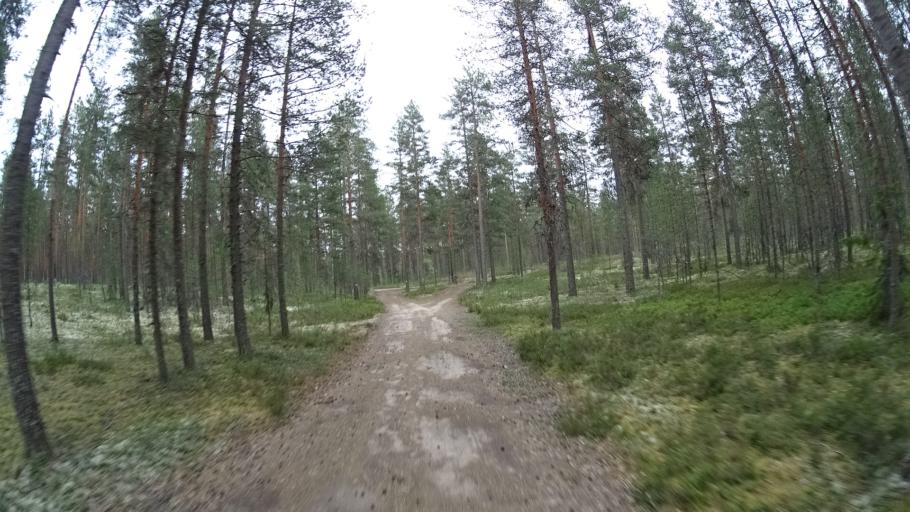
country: FI
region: Satakunta
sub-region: Pohjois-Satakunta
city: Jaemijaervi
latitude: 61.7640
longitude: 22.7518
